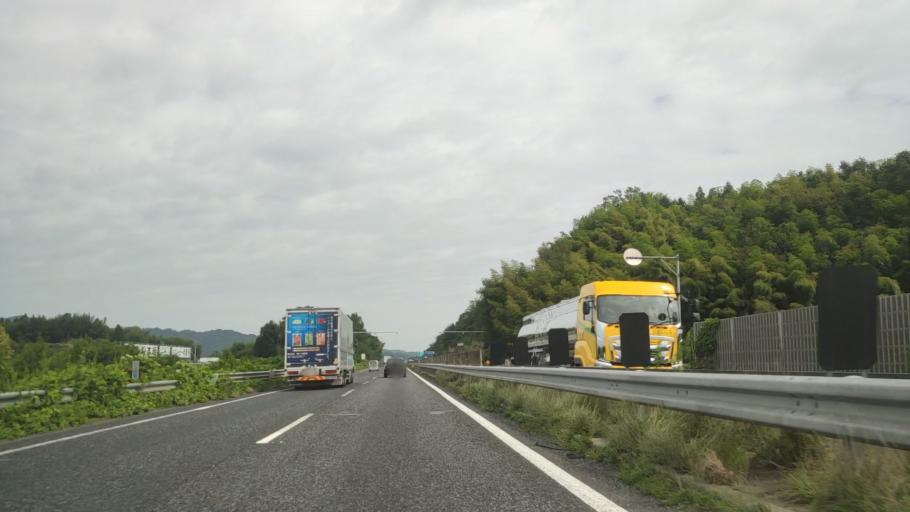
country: JP
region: Mie
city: Ueno-ebisumachi
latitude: 34.7832
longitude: 136.1591
